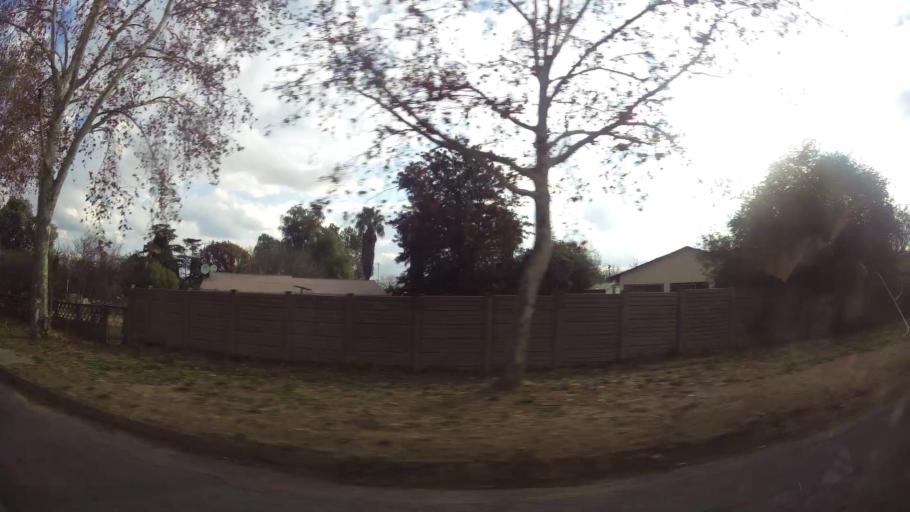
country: ZA
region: Orange Free State
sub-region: Fezile Dabi District Municipality
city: Sasolburg
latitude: -26.8225
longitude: 27.8240
